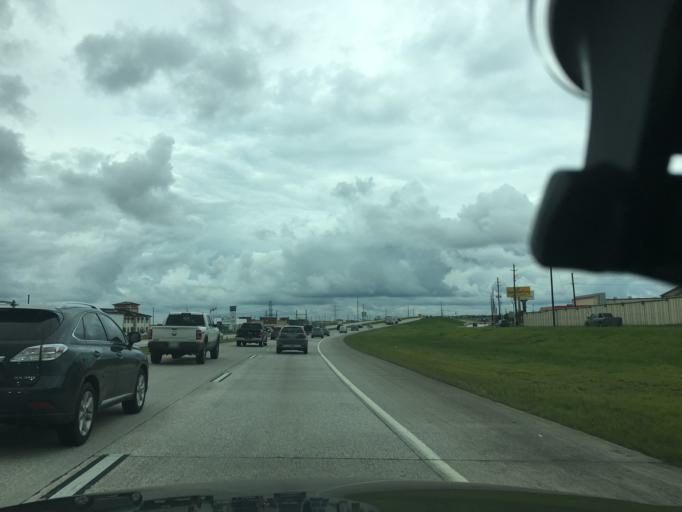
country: US
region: Texas
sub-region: Harris County
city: Tomball
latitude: 30.0849
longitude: -95.5348
